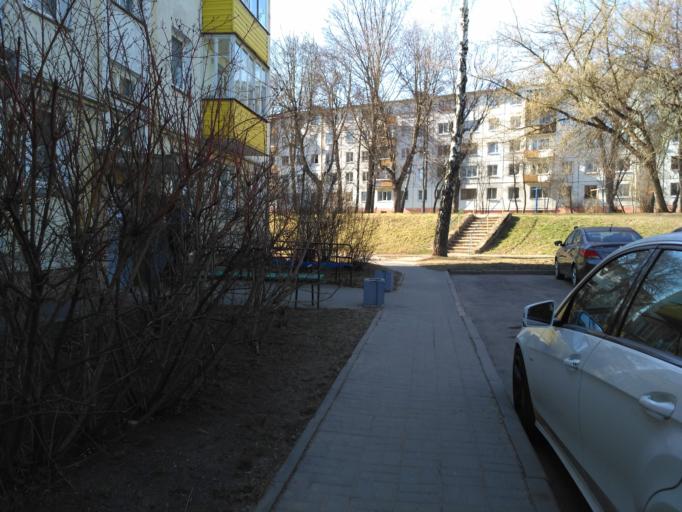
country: BY
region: Minsk
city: Minsk
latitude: 53.9038
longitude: 27.5086
